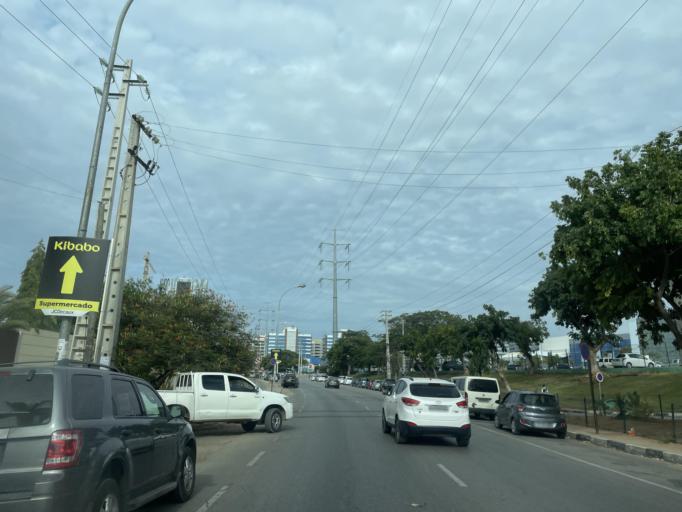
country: AO
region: Luanda
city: Luanda
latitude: -8.9235
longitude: 13.1839
